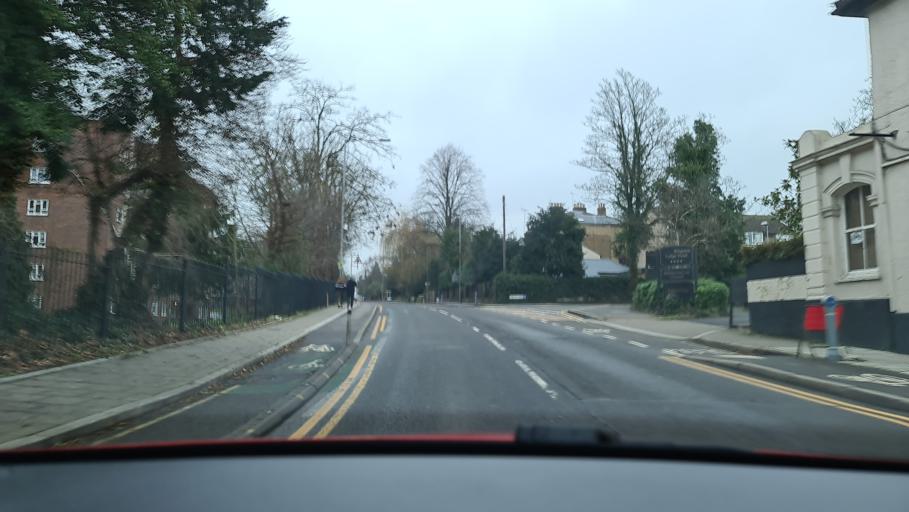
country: GB
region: England
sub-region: Greater London
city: Kingston upon Thames
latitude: 51.4188
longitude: -0.2793
